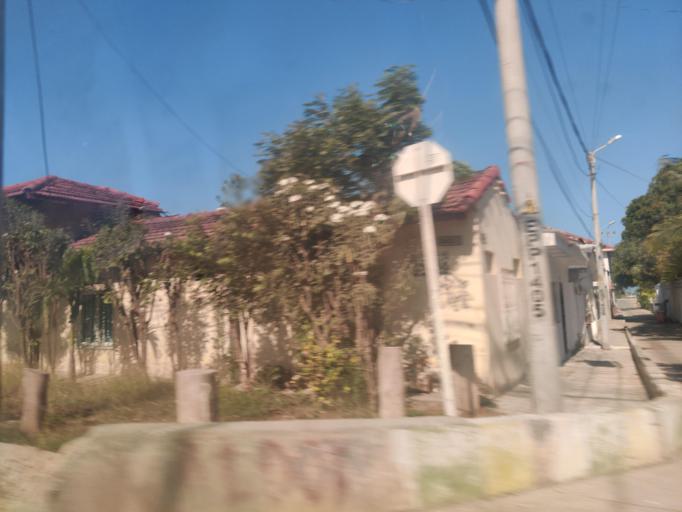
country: CO
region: Atlantico
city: Puerto Colombia
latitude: 10.9965
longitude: -74.9533
